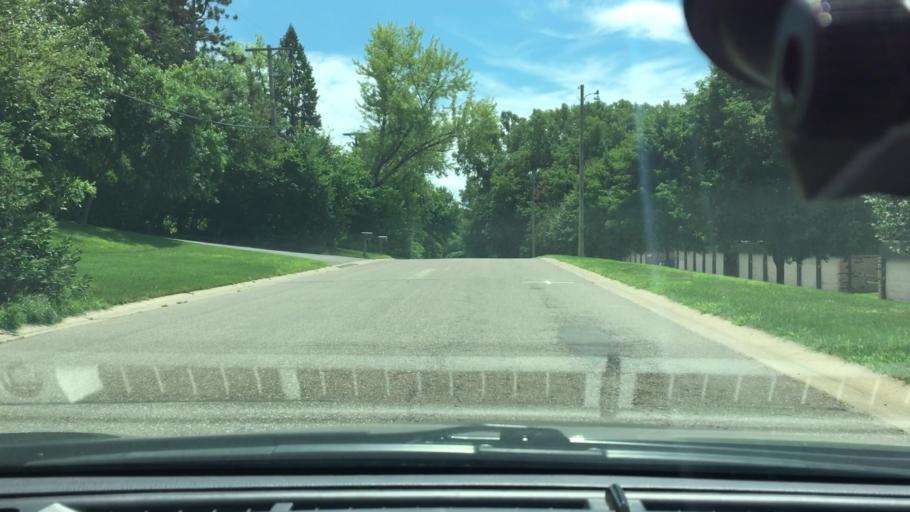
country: US
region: Minnesota
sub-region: Hennepin County
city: New Hope
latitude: 45.0068
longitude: -93.4032
